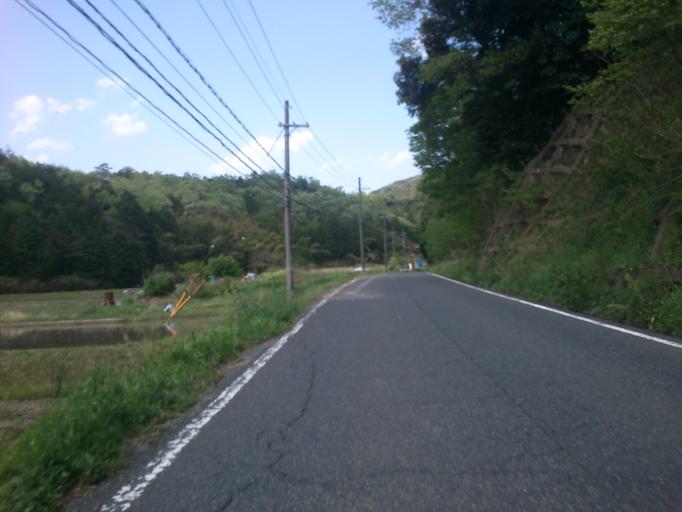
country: JP
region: Kyoto
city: Miyazu
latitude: 35.6830
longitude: 135.1109
